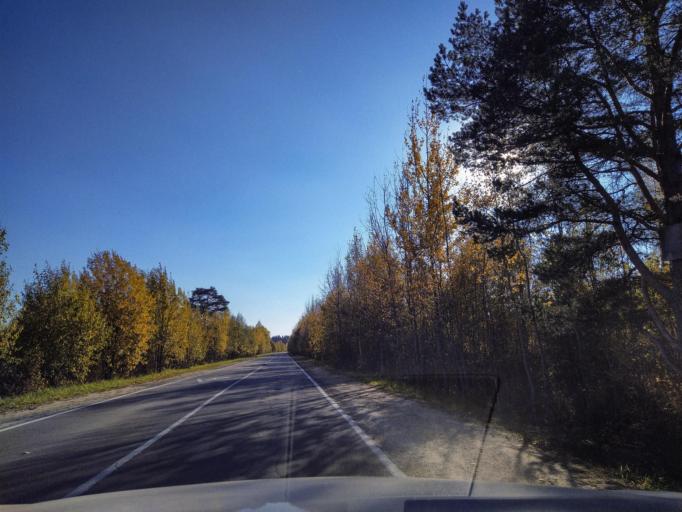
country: RU
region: Leningrad
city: Siverskiy
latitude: 59.3161
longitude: 30.0338
